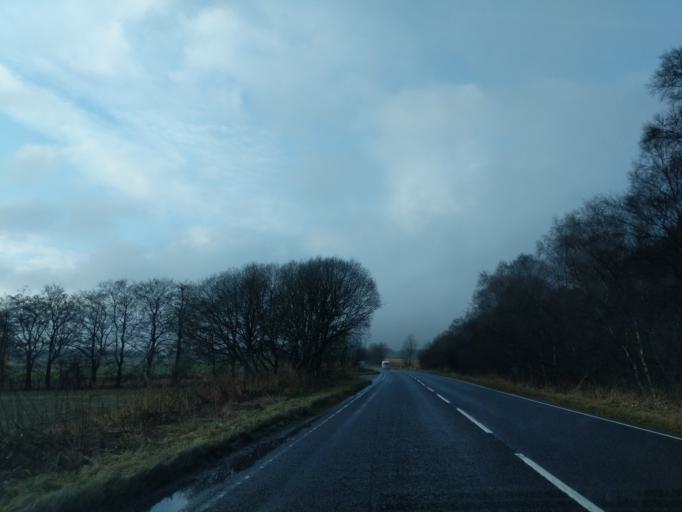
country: GB
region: Scotland
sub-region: Perth and Kinross
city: Kinross
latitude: 56.2013
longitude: -3.4985
